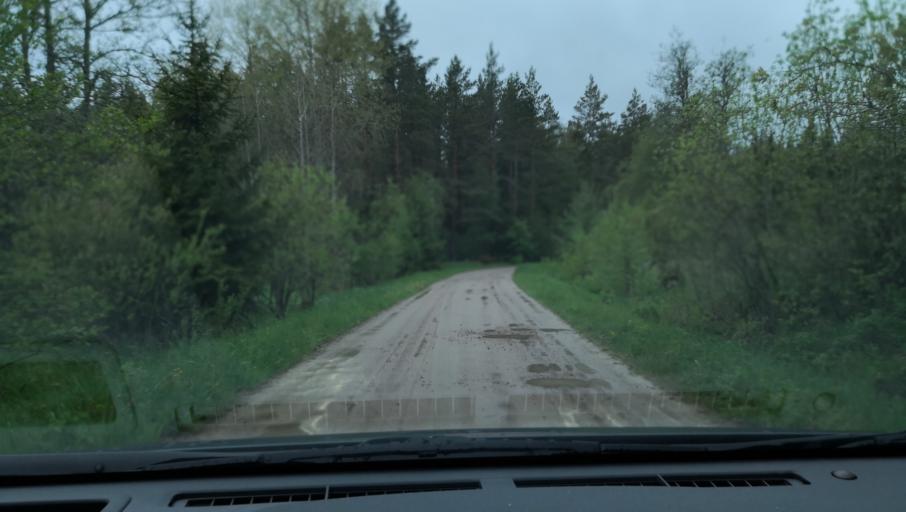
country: SE
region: Uppsala
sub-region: Enkopings Kommun
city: Orsundsbro
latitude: 59.9146
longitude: 17.3501
